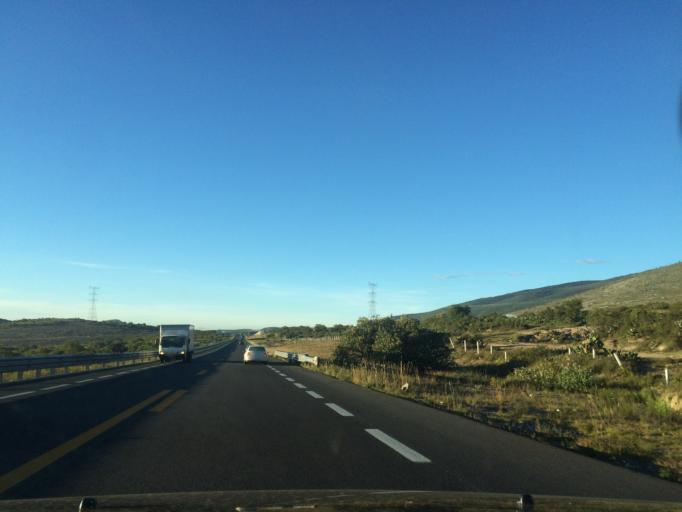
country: MX
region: Puebla
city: Morelos Canada
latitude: 18.7094
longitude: -97.4688
